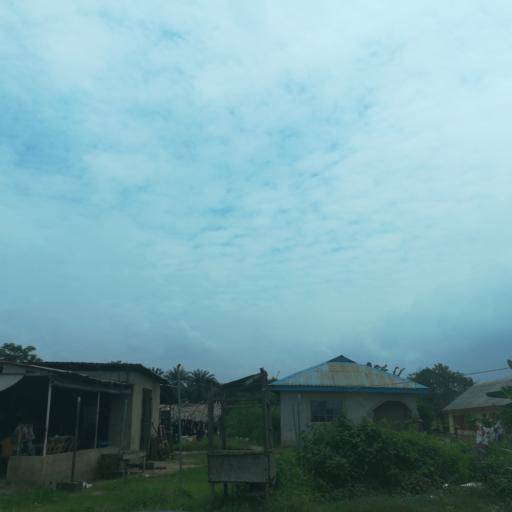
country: NG
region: Lagos
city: Ejirin
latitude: 6.6611
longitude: 3.7940
